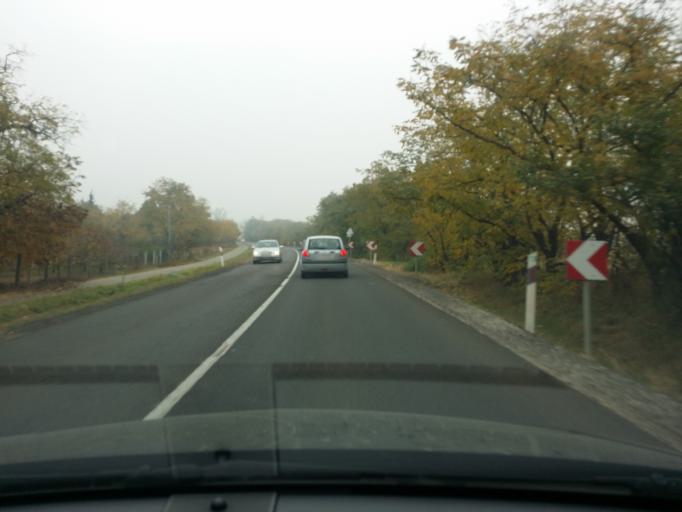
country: HU
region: Szabolcs-Szatmar-Bereg
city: Nyirpazony
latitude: 48.0006
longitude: 21.8181
